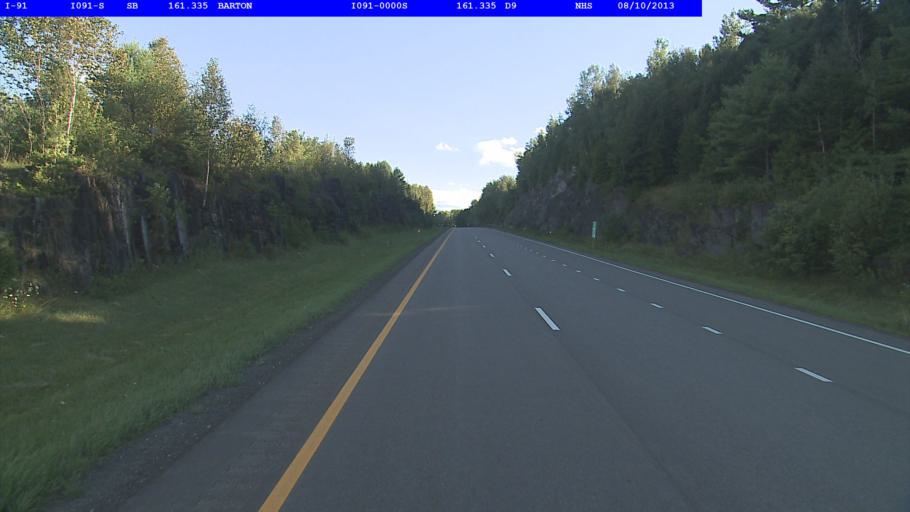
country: US
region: Vermont
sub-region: Orleans County
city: Newport
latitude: 44.8054
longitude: -72.2131
